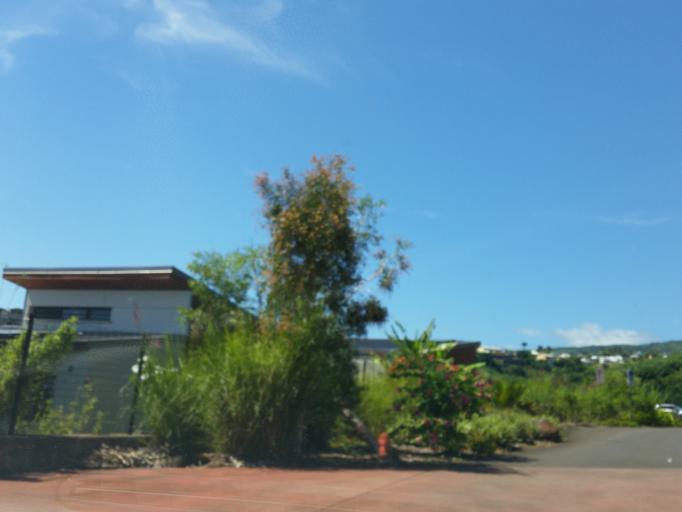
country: RE
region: Reunion
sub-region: Reunion
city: Sainte-Marie
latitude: -20.9155
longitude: 55.5204
